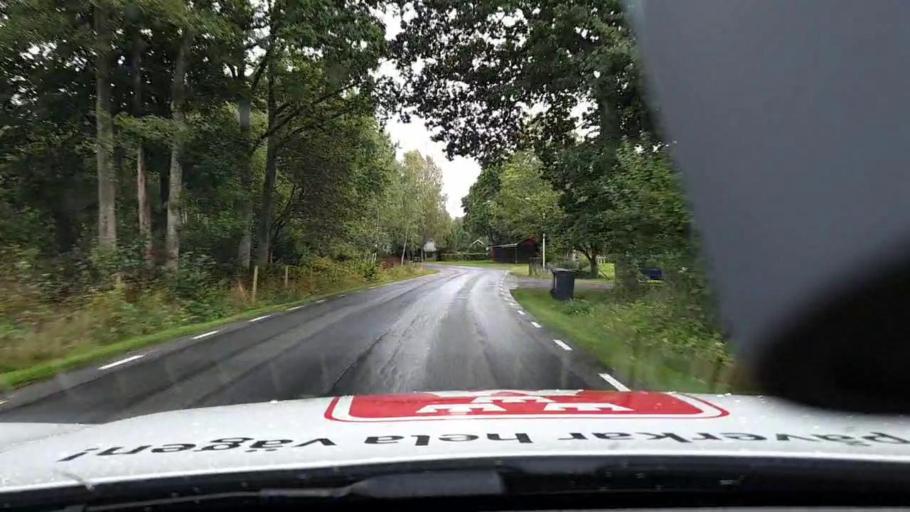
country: SE
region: Skane
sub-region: Hassleholms Kommun
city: Vinslov
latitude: 56.0385
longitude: 13.8729
